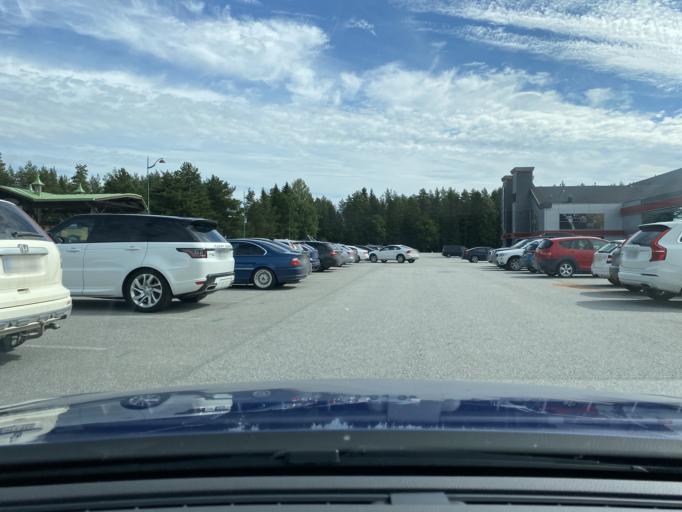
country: FI
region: Southern Ostrobothnia
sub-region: Seinaejoki
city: Alahaermae
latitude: 63.2275
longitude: 22.8588
